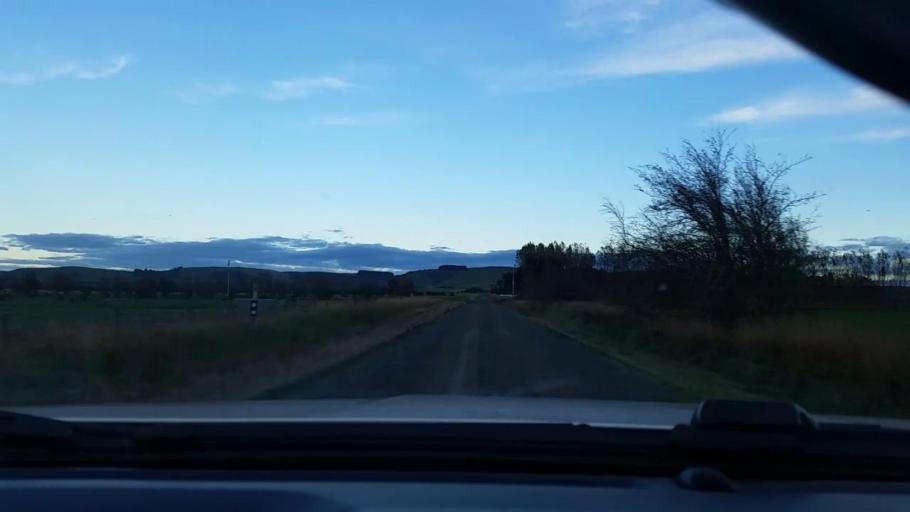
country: NZ
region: Southland
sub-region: Southland District
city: Winton
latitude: -46.1067
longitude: 168.4489
